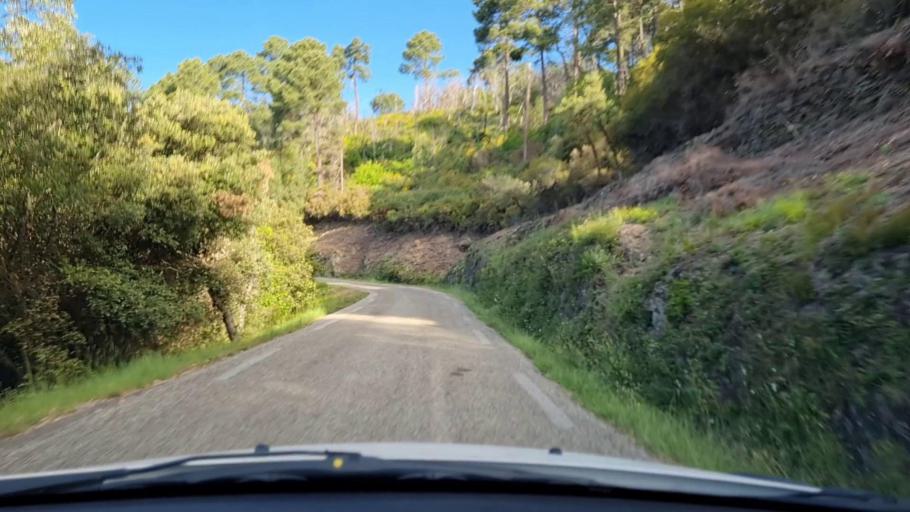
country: FR
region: Languedoc-Roussillon
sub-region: Departement du Gard
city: Branoux-les-Taillades
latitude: 44.1842
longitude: 4.0059
